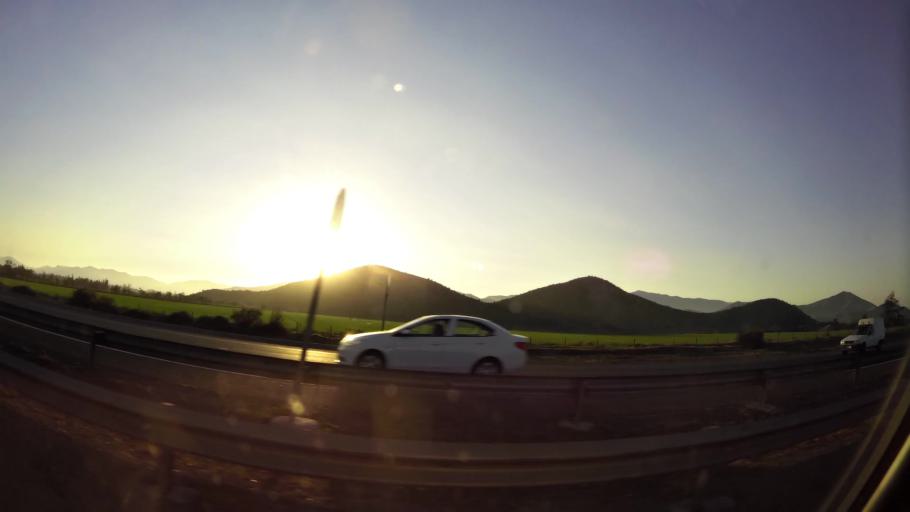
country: CL
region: Santiago Metropolitan
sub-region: Provincia de Talagante
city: Penaflor
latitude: -33.5406
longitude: -70.8033
